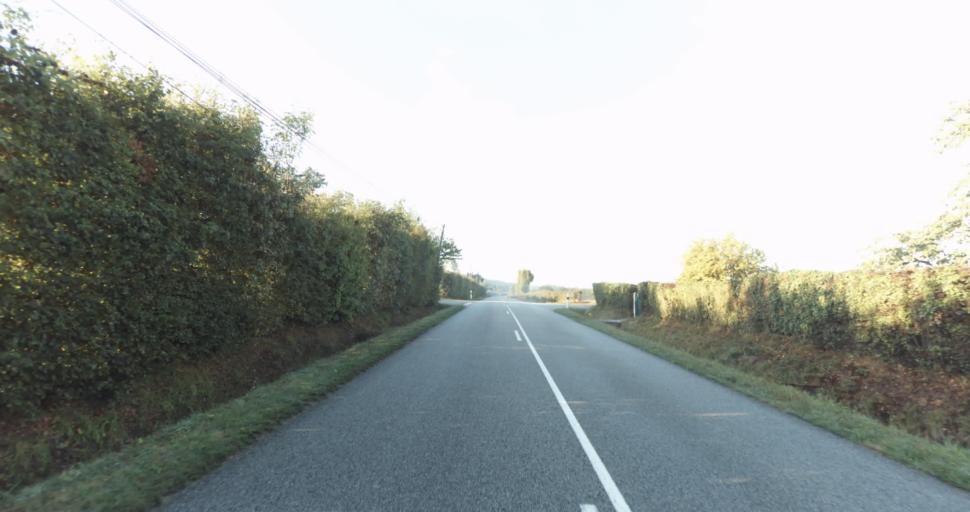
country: FR
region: Lower Normandy
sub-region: Departement de l'Orne
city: Vimoutiers
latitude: 48.9160
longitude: 0.1502
